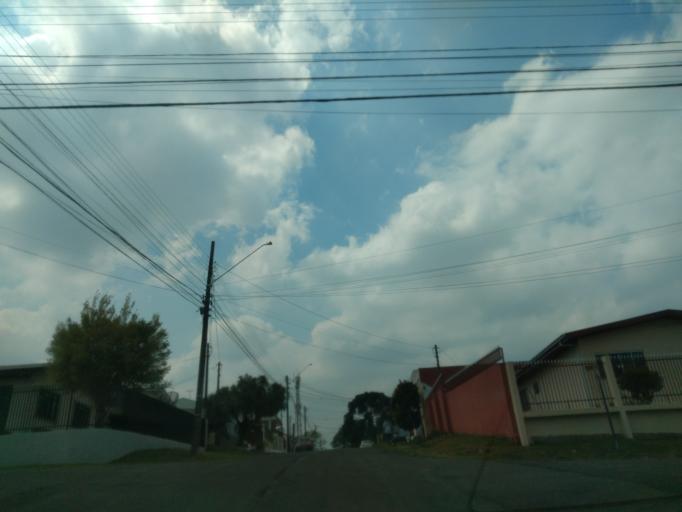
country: BR
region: Parana
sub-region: Guarapuava
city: Guarapuava
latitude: -25.3810
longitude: -51.4817
